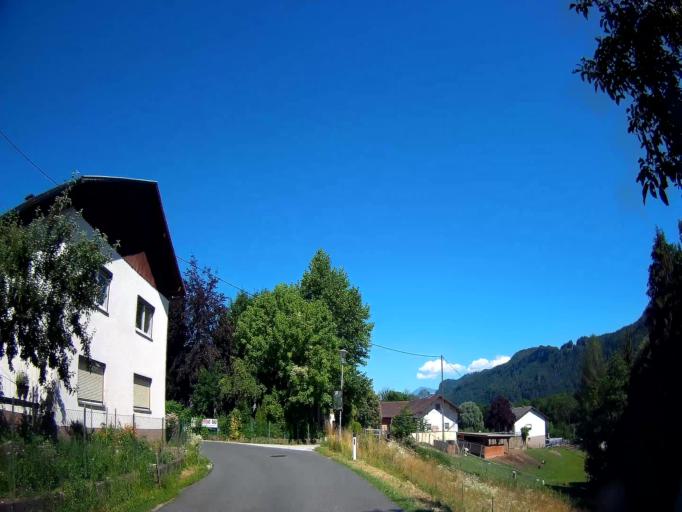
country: AT
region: Carinthia
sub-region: Politischer Bezirk Klagenfurt Land
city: Grafenstein
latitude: 46.6127
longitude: 14.4429
